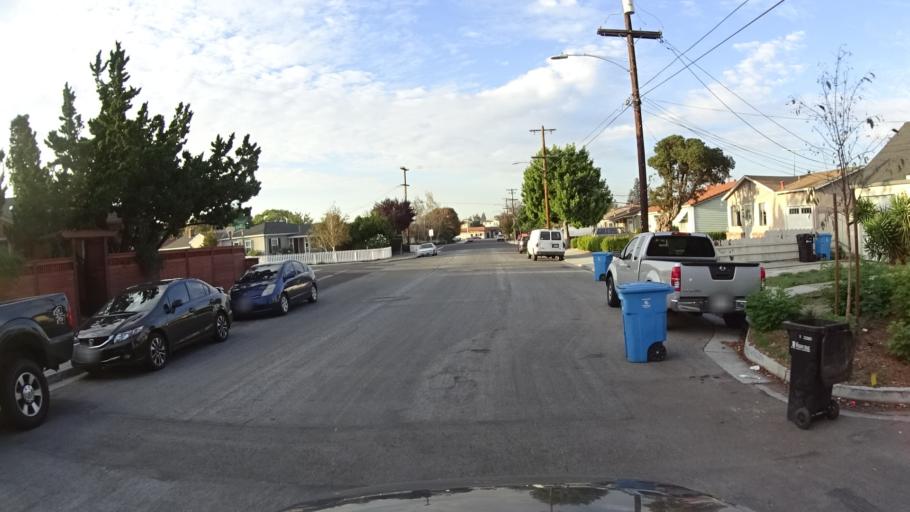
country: US
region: California
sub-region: Santa Clara County
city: Santa Clara
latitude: 37.3504
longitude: -121.9561
